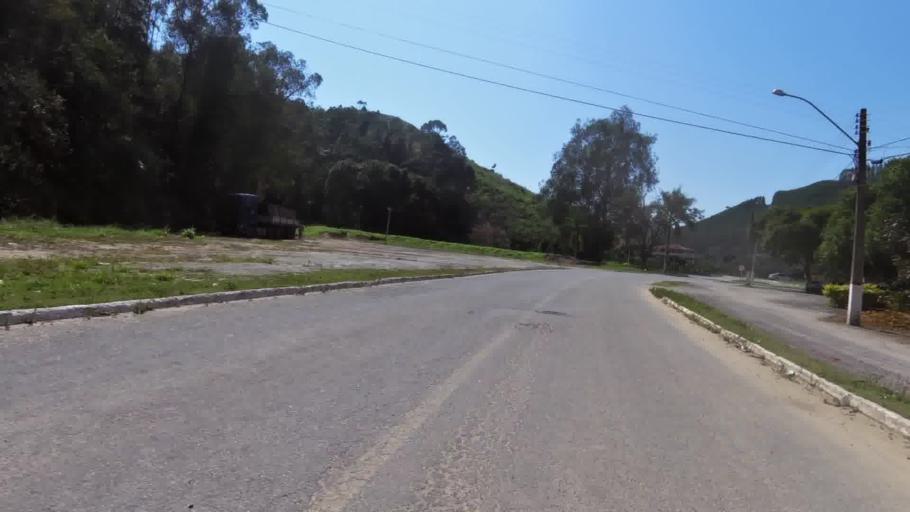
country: BR
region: Espirito Santo
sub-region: Marechal Floriano
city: Marechal Floriano
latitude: -20.4200
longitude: -40.8783
